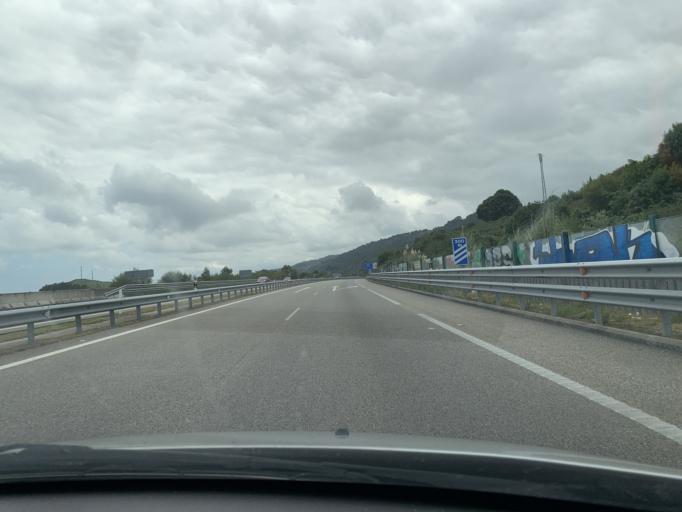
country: ES
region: Asturias
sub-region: Province of Asturias
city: Llanes
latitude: 43.3997
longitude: -4.6633
